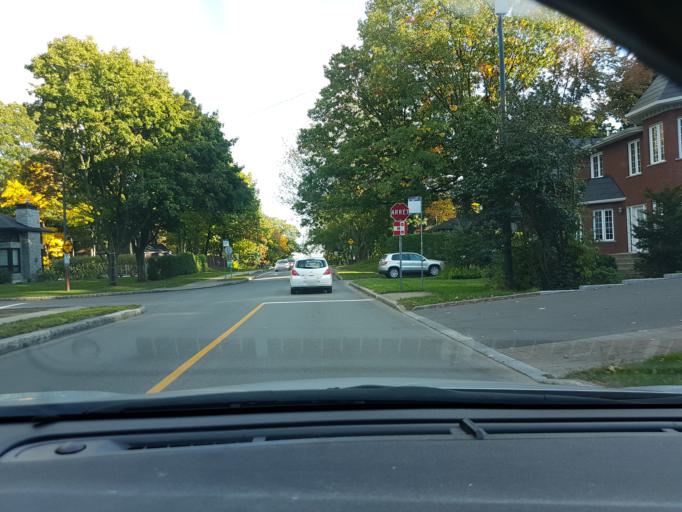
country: CA
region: Quebec
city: Quebec
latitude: 46.7721
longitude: -71.2701
